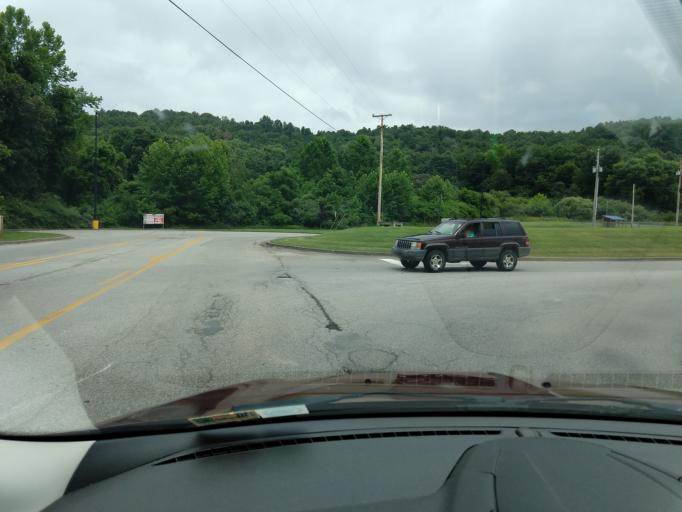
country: US
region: West Virginia
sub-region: Jackson County
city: Ripley
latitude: 38.8302
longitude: -81.7223
